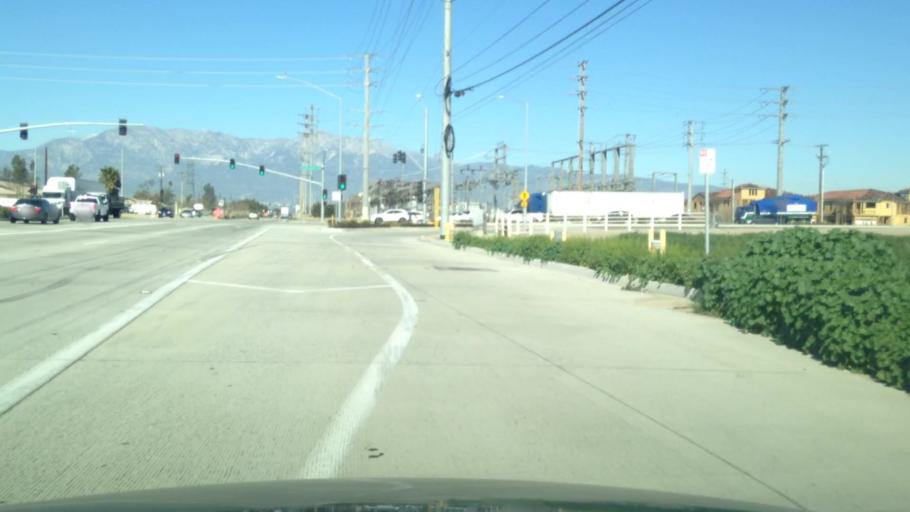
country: US
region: California
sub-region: Riverside County
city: Mira Loma
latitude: 33.9963
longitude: -117.5932
